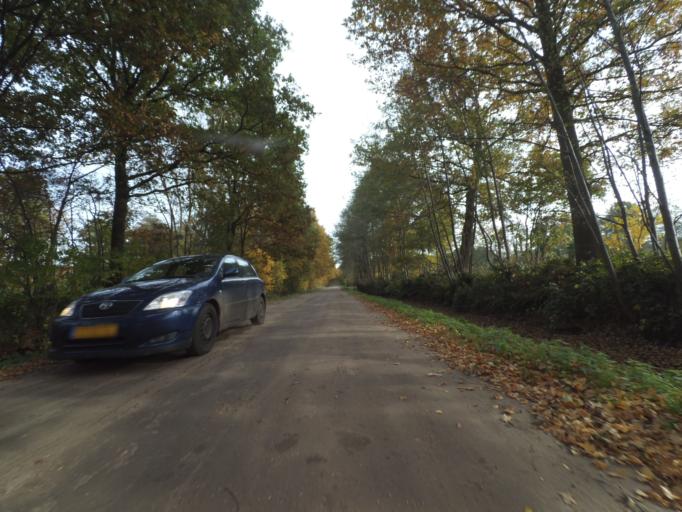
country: NL
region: Gelderland
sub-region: Gemeente Ede
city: Lunteren
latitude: 52.1024
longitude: 5.6159
